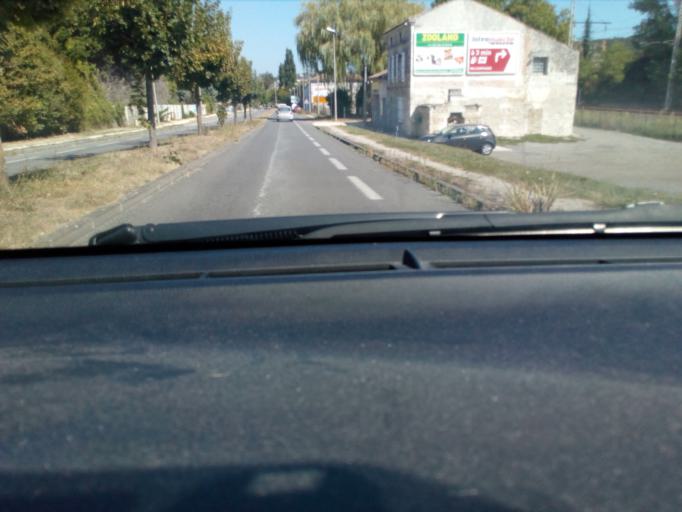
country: FR
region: Poitou-Charentes
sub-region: Departement de la Charente
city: Saint-Michel
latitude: 45.6345
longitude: 0.1249
